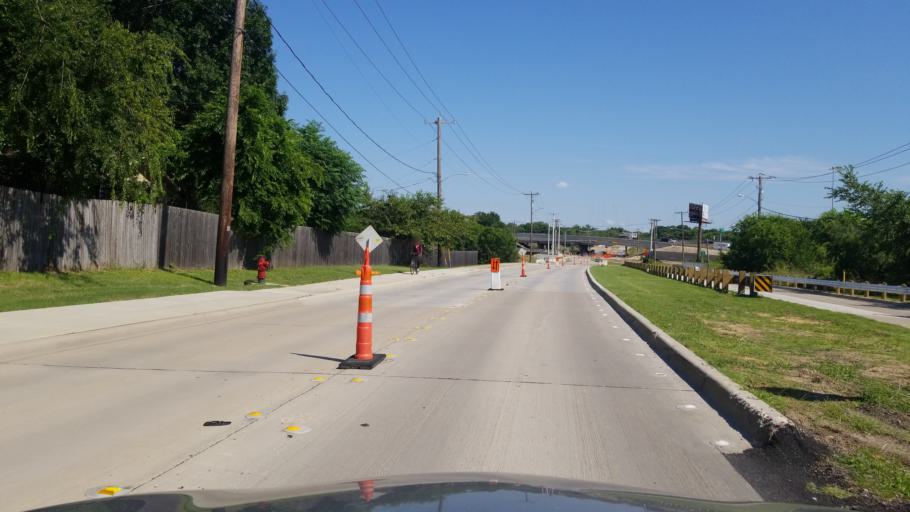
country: US
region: Texas
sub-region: Dallas County
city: Grand Prairie
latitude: 32.6788
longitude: -97.0179
